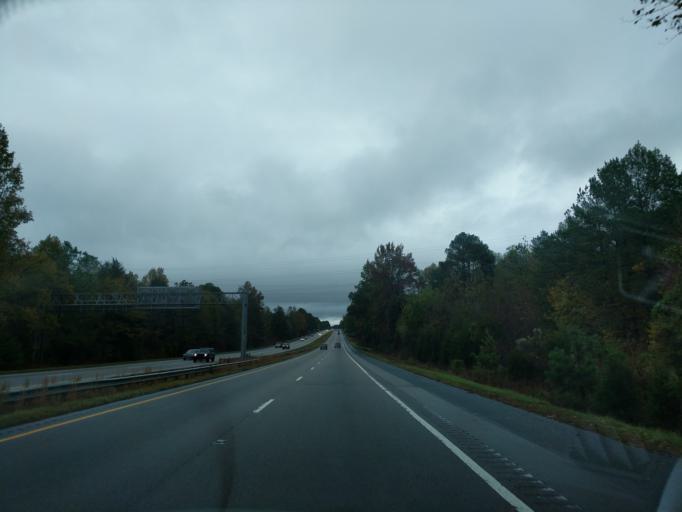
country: US
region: North Carolina
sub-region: Durham County
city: Gorman
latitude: 36.0506
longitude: -78.8074
